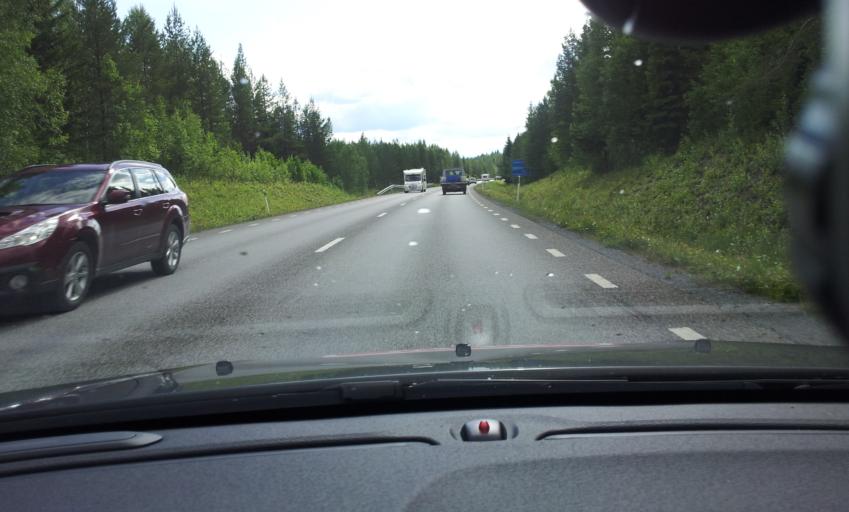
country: SE
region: Jaemtland
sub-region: Krokoms Kommun
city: Valla
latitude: 63.3118
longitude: 13.9265
